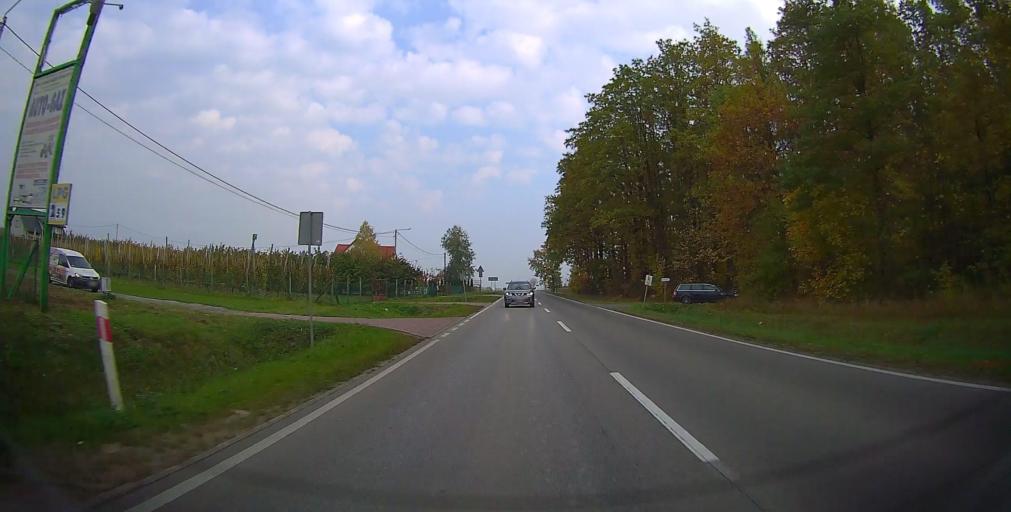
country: PL
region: Masovian Voivodeship
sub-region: Powiat grojecki
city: Belsk Duzy
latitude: 51.7974
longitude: 20.7871
